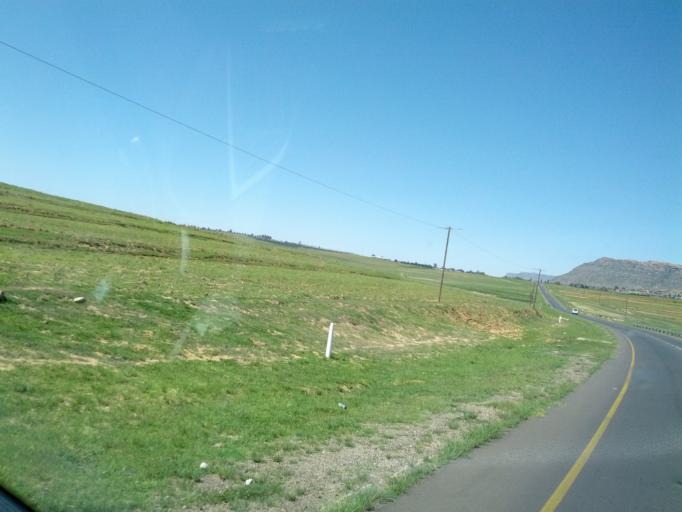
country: LS
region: Maseru
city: Maseru
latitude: -29.4626
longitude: 27.5382
